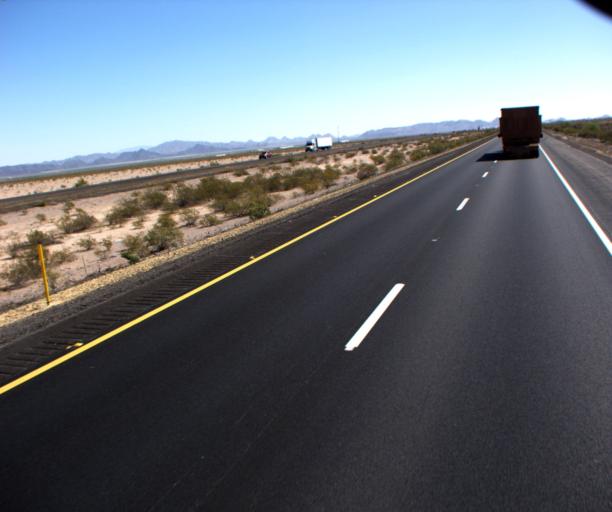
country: US
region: Arizona
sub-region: La Paz County
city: Salome
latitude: 33.6363
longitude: -113.8056
